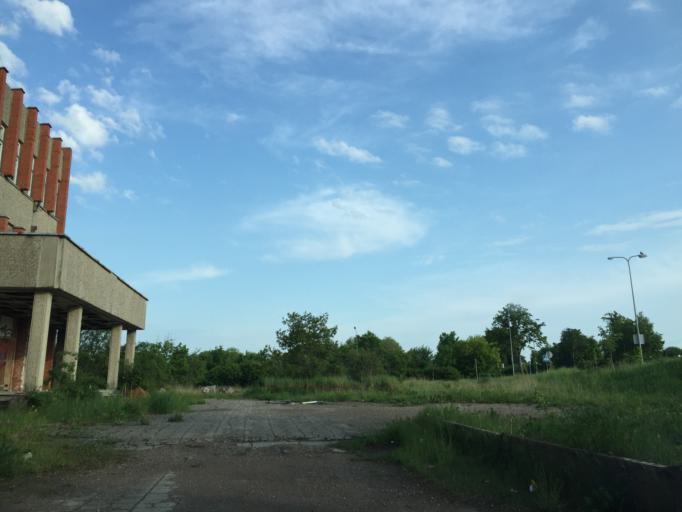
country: LT
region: Klaipedos apskritis
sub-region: Klaipeda
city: Klaipeda
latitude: 55.7538
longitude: 21.1331
